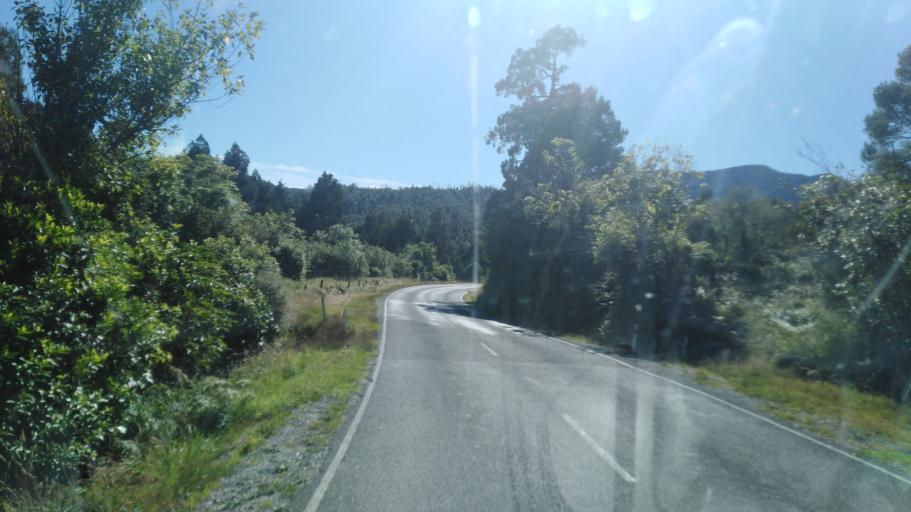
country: NZ
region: West Coast
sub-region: Buller District
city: Westport
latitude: -41.5291
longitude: 171.9751
